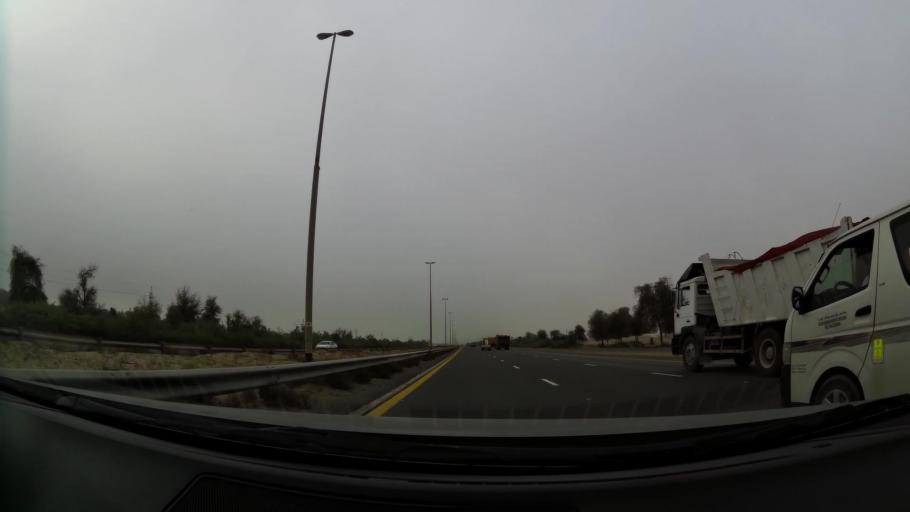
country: AE
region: Dubai
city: Dubai
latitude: 25.0751
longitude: 55.4022
